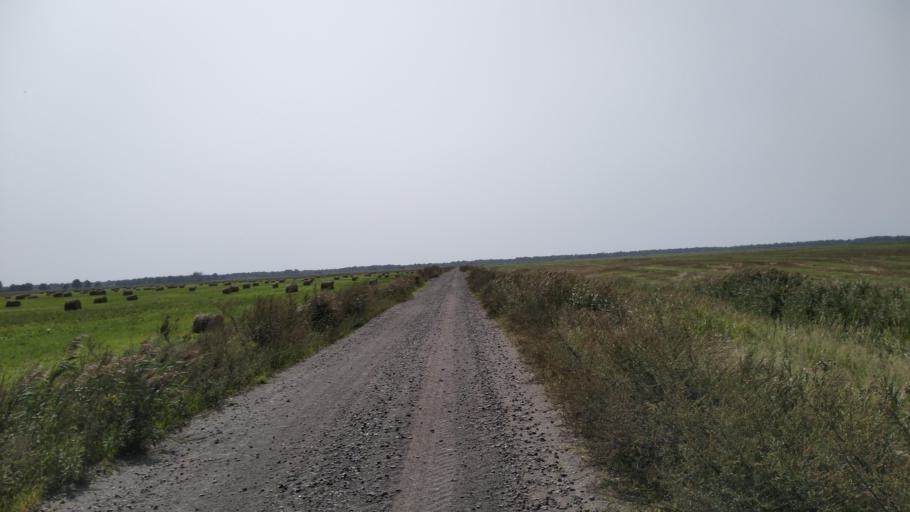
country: BY
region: Brest
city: Davyd-Haradok
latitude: 51.9913
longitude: 27.1761
